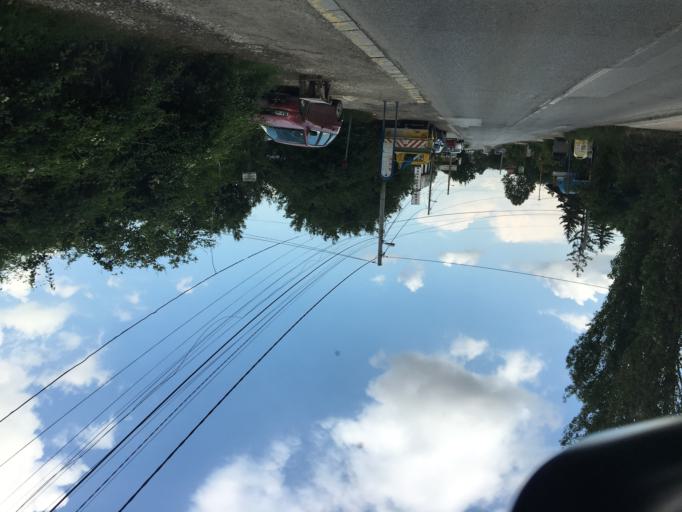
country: BG
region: Sofia-Capital
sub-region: Stolichna Obshtina
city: Sofia
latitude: 42.6348
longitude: 23.3540
